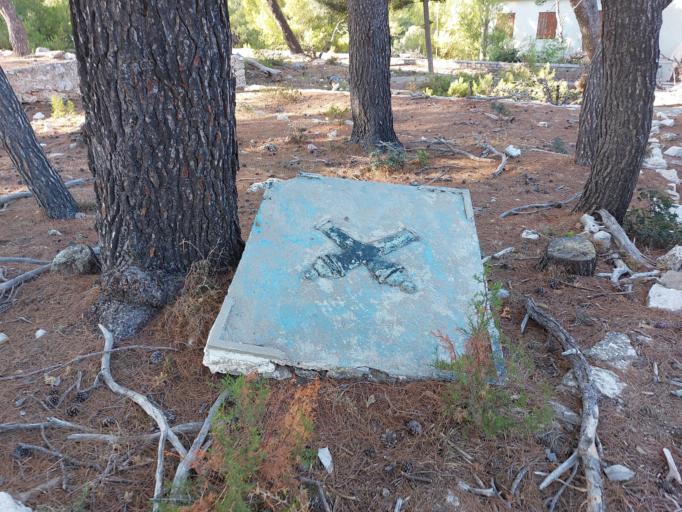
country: HR
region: Dubrovacko-Neretvanska
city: Smokvica
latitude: 42.7320
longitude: 16.8402
